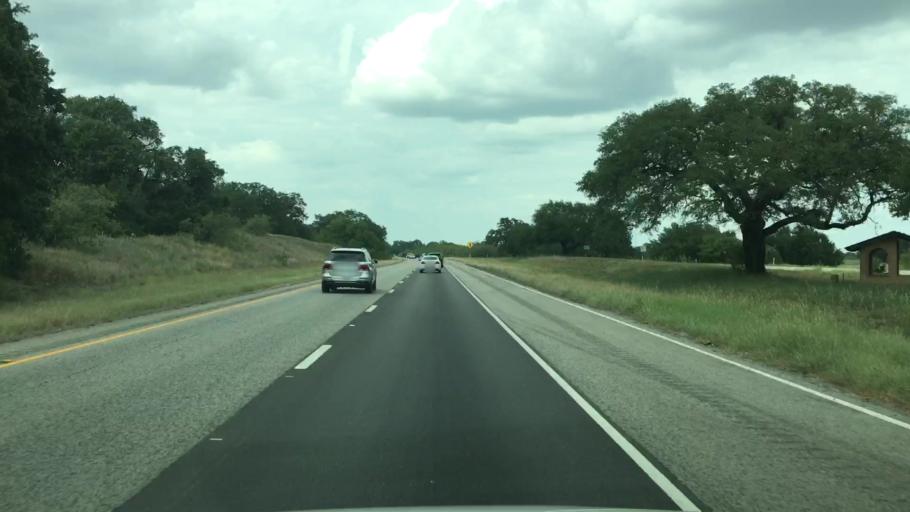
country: US
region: Texas
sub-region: Atascosa County
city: Pleasanton
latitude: 29.0353
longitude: -98.4322
